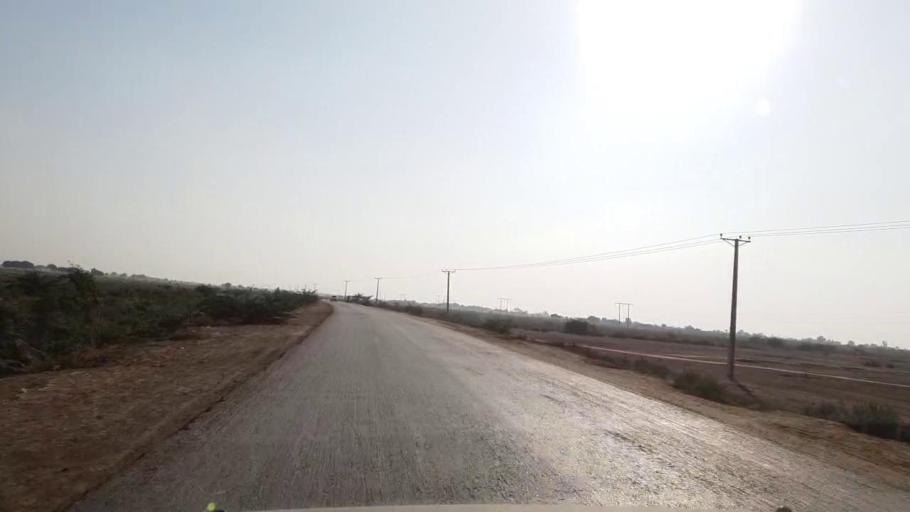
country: PK
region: Sindh
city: Bulri
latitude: 24.9186
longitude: 68.3501
